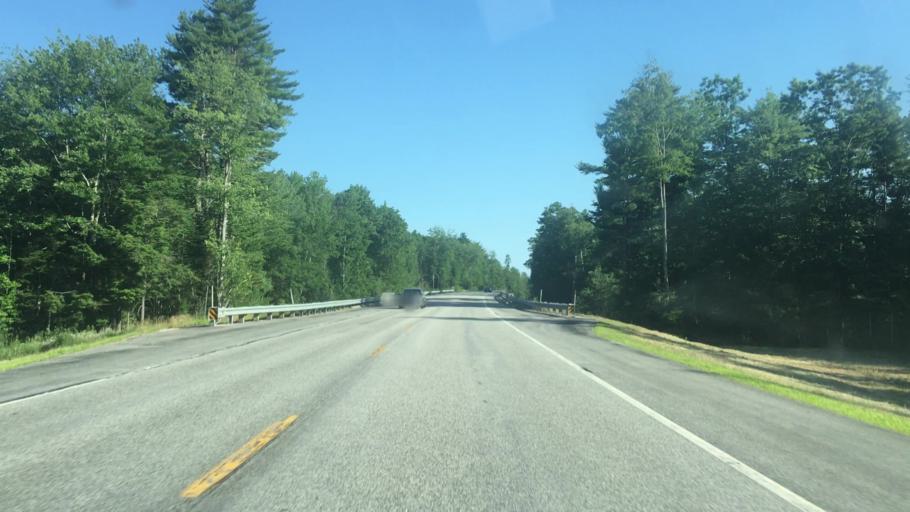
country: US
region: Maine
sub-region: Cumberland County
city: Gorham
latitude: 43.6584
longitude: -70.4495
